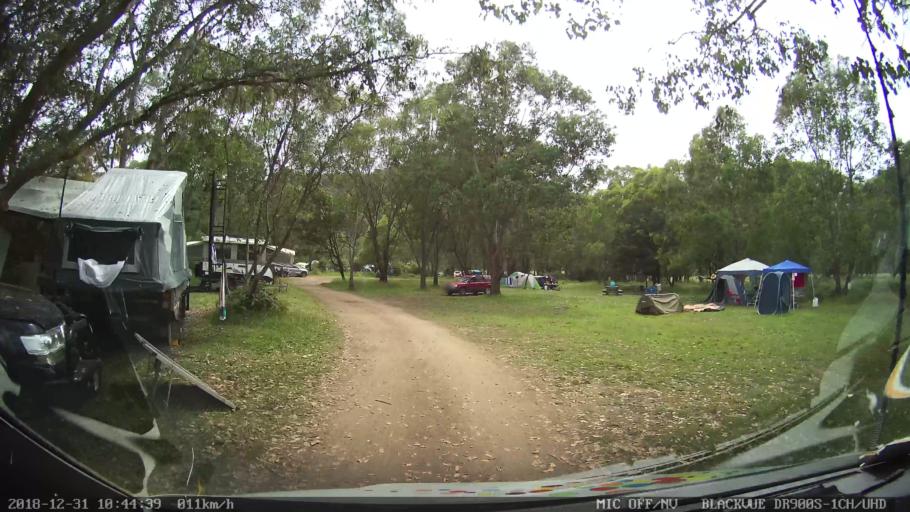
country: AU
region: New South Wales
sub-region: Snowy River
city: Jindabyne
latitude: -36.3786
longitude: 148.1785
